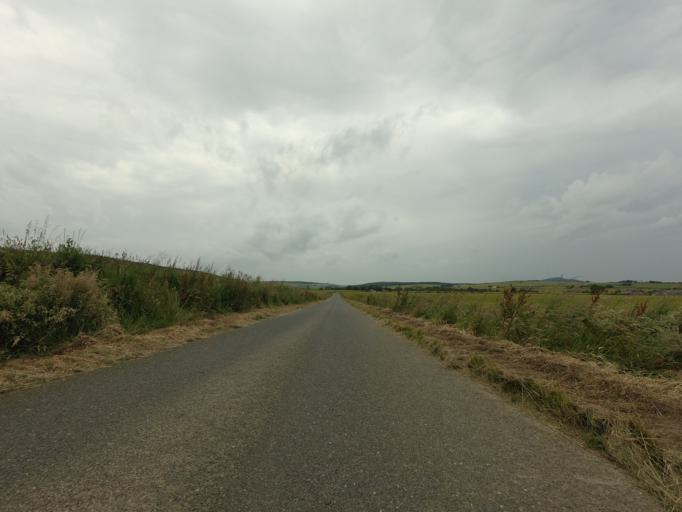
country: GB
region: Scotland
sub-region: Aberdeenshire
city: Portsoy
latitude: 57.6650
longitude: -2.7314
